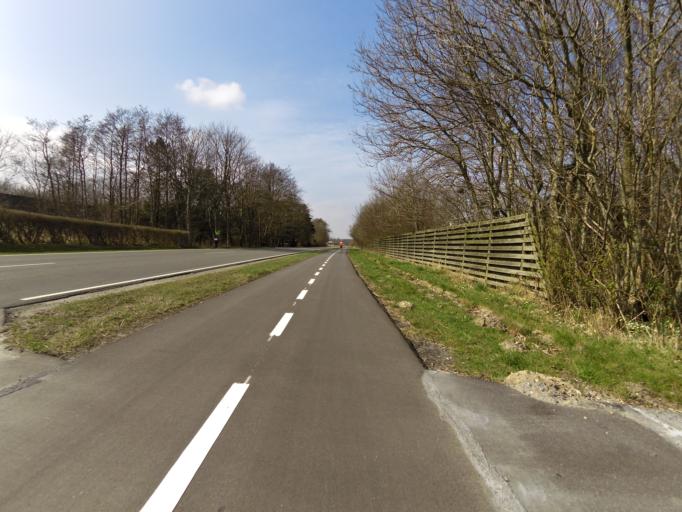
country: DK
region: Central Jutland
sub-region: Struer Kommune
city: Struer
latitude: 56.4705
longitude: 8.6313
